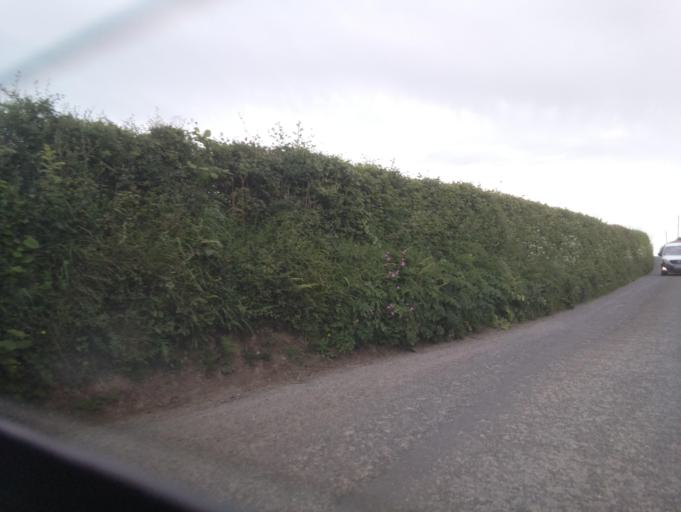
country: GB
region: England
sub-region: Devon
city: Dartmouth
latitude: 50.3197
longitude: -3.6356
